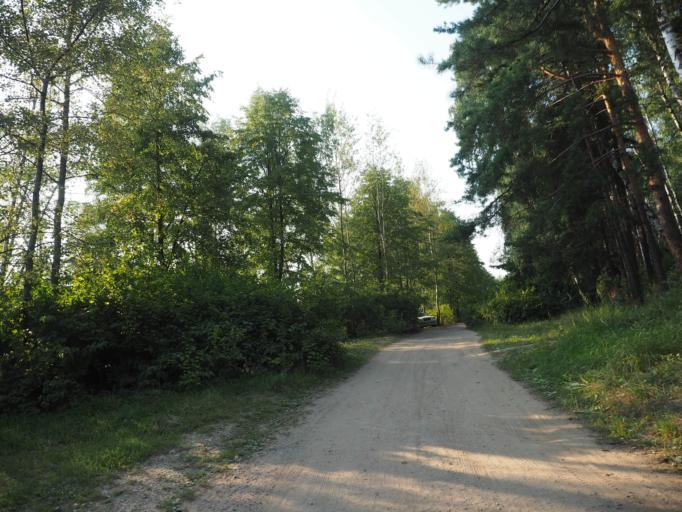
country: RU
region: Moskovskaya
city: Dzerzhinskiy
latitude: 55.6365
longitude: 37.8913
